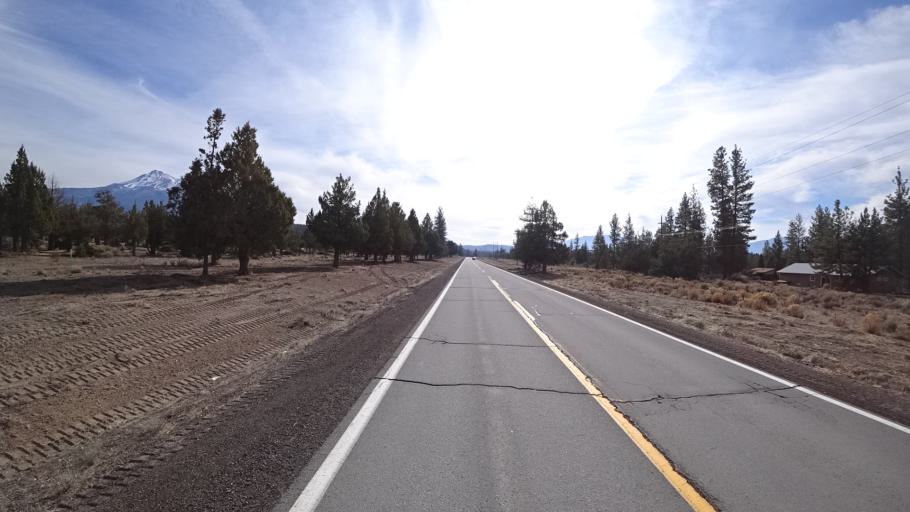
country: US
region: California
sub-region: Siskiyou County
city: Weed
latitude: 41.5348
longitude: -122.3647
